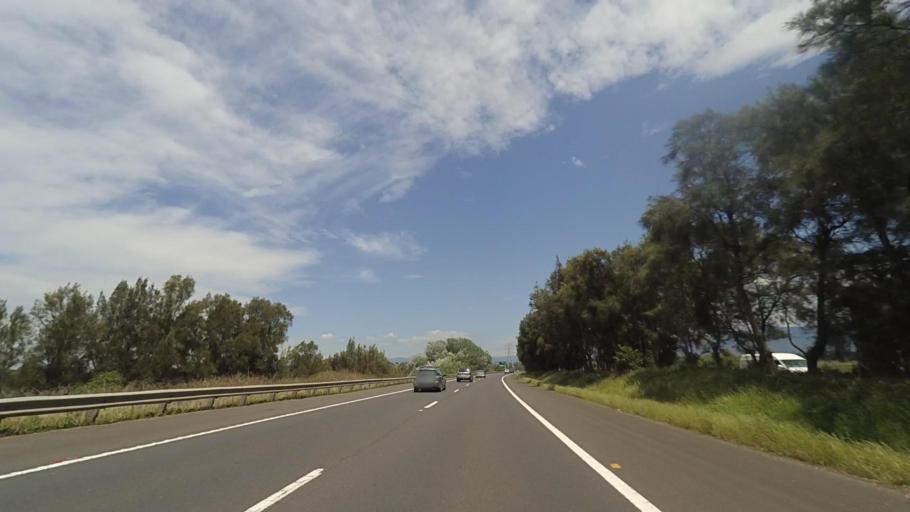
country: AU
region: New South Wales
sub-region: Wollongong
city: Koonawarra
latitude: -34.4823
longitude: 150.8218
